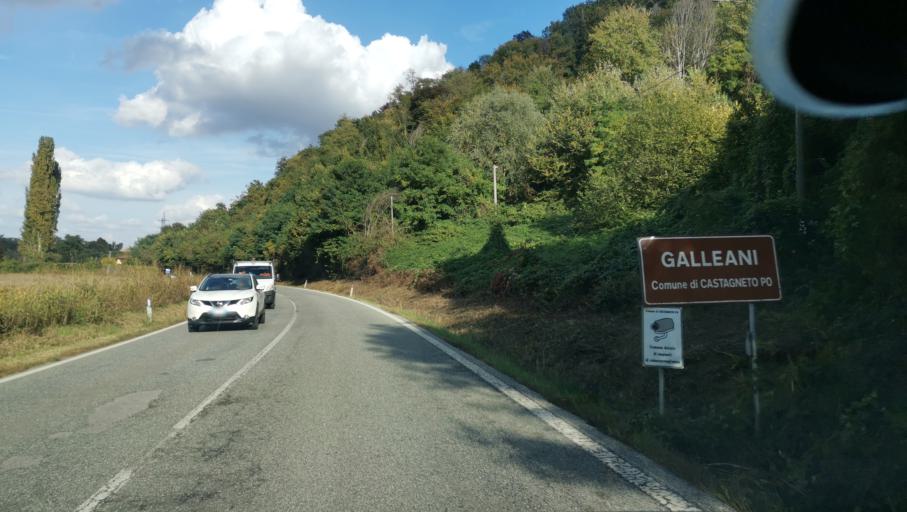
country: IT
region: Piedmont
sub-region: Provincia di Torino
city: Castagneto Po
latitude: 45.1719
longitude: 7.8762
